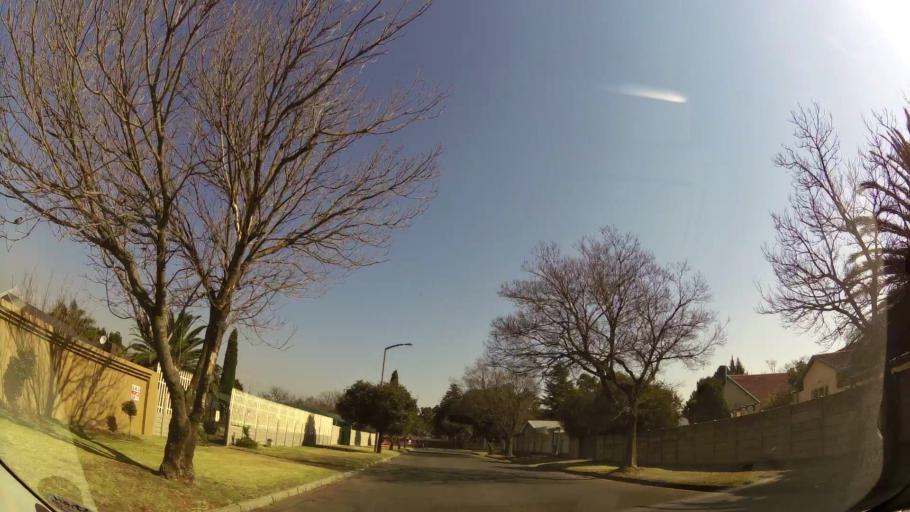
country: ZA
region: Gauteng
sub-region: Ekurhuleni Metropolitan Municipality
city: Boksburg
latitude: -26.1634
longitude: 28.2655
